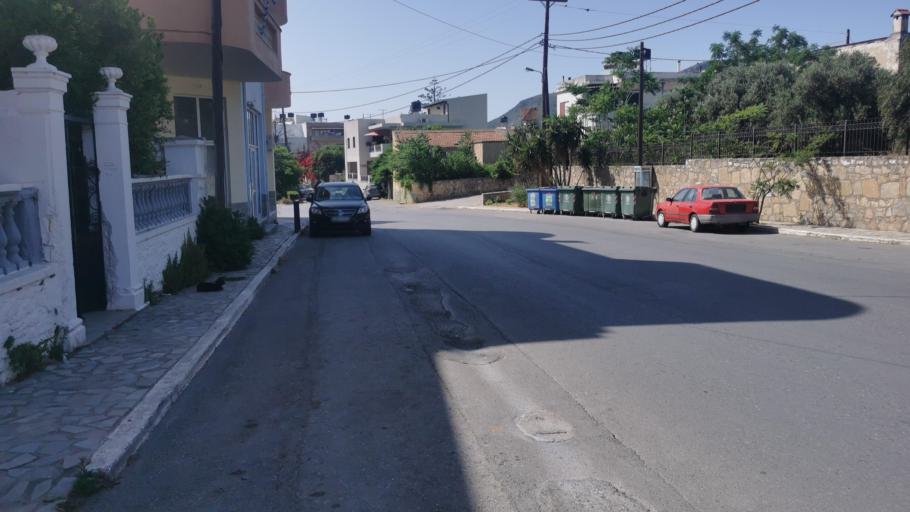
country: GR
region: Crete
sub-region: Nomos Lasithiou
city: Neapoli
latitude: 35.2583
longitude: 25.6073
